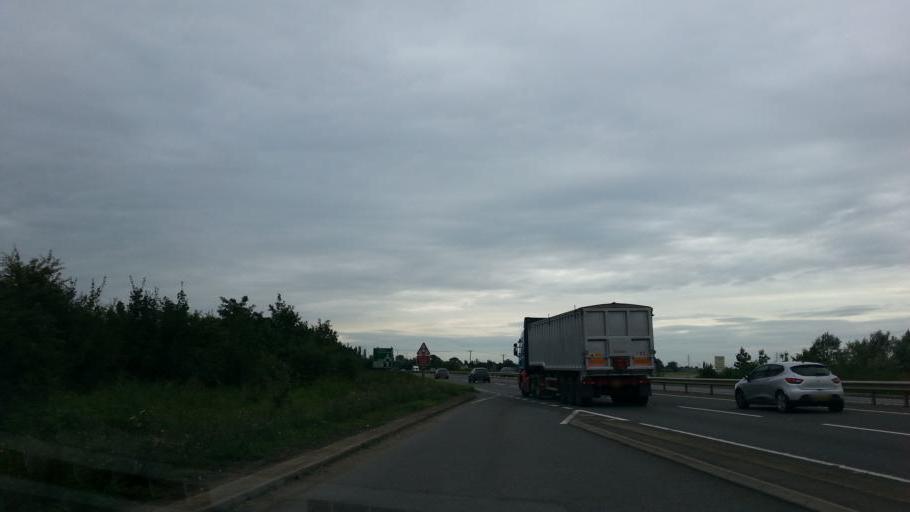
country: GB
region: England
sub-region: Peterborough
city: Thorney
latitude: 52.6239
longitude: -0.1159
